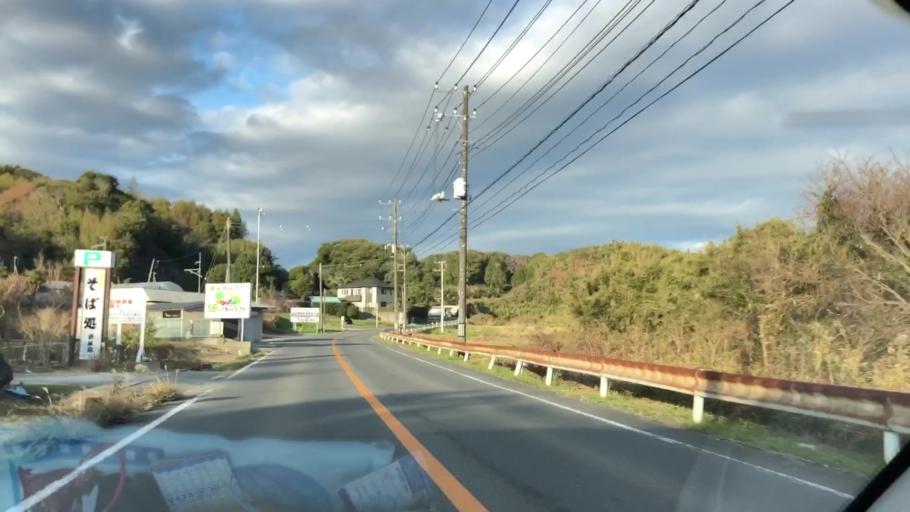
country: JP
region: Chiba
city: Tateyama
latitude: 34.9867
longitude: 139.9406
